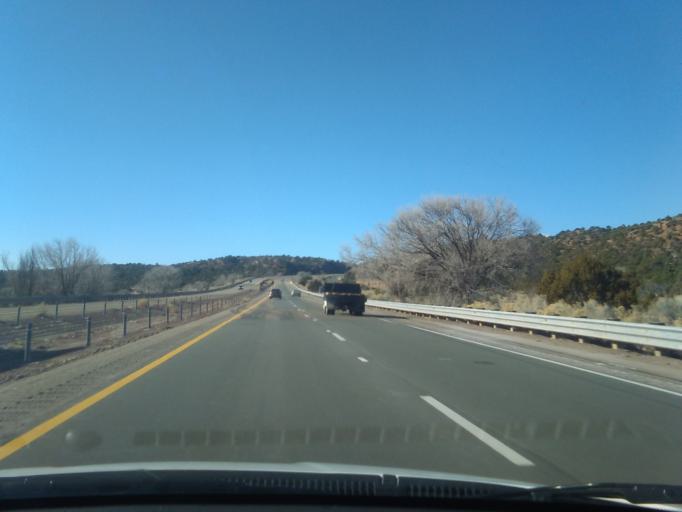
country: US
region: New Mexico
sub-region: Santa Fe County
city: Eldorado at Santa Fe
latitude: 35.5407
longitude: -105.8441
